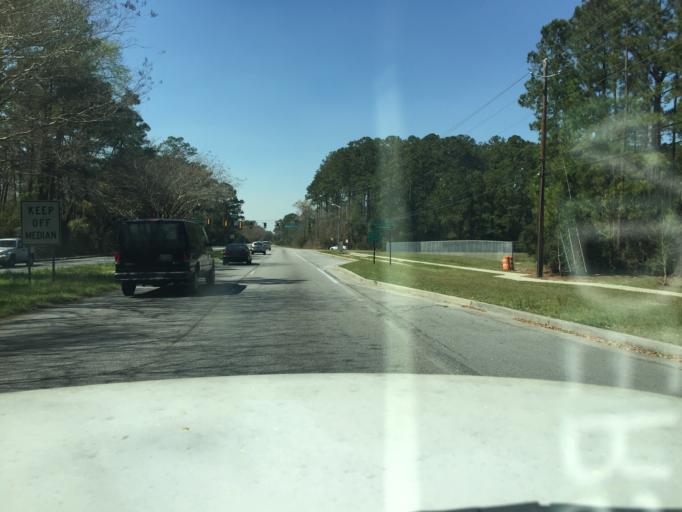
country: US
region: Georgia
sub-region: Chatham County
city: Whitemarsh Island
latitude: 32.0351
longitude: -81.0085
